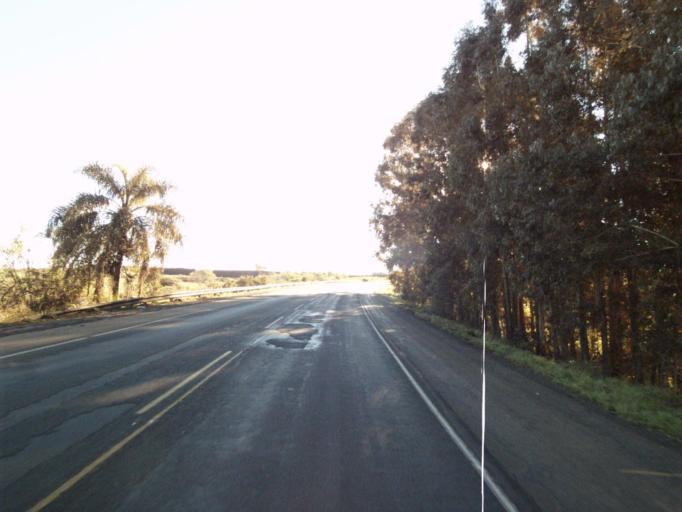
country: BR
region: Santa Catarina
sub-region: Chapeco
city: Chapeco
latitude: -26.9994
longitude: -52.7176
